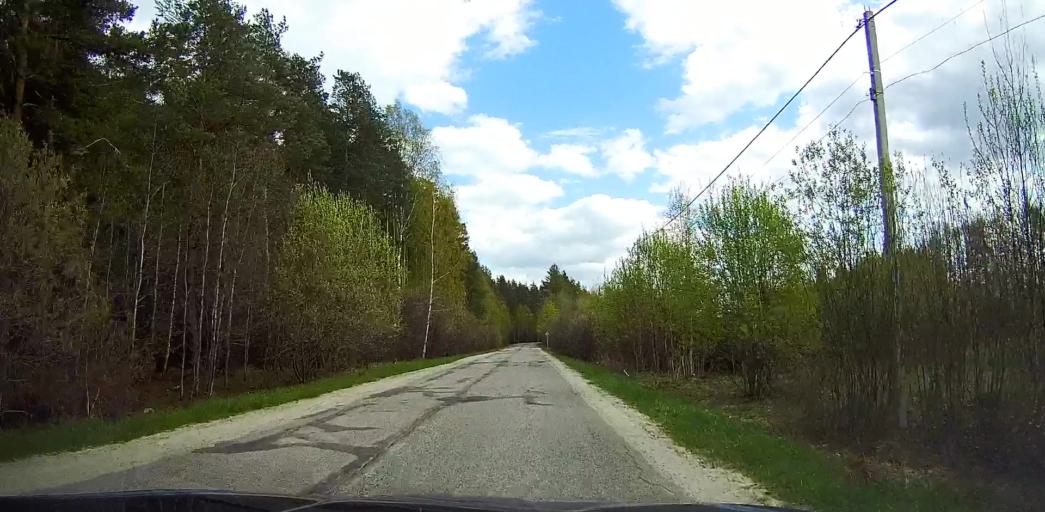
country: RU
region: Moskovskaya
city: Davydovo
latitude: 55.6452
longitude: 38.7709
